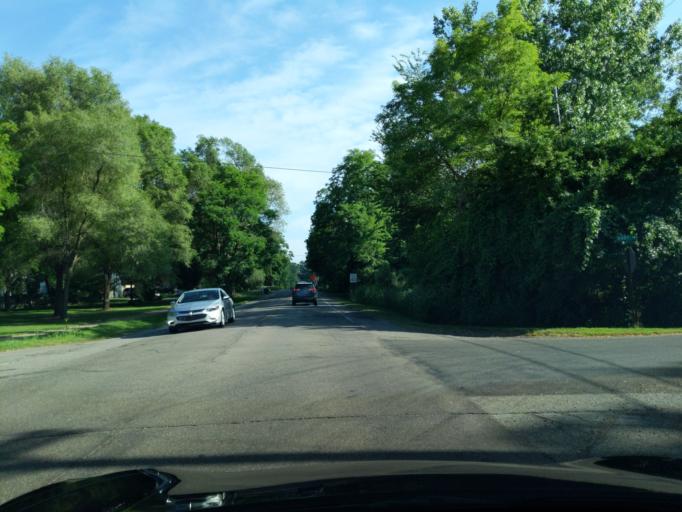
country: US
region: Michigan
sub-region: Ingham County
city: Okemos
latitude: 42.7445
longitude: -84.4277
